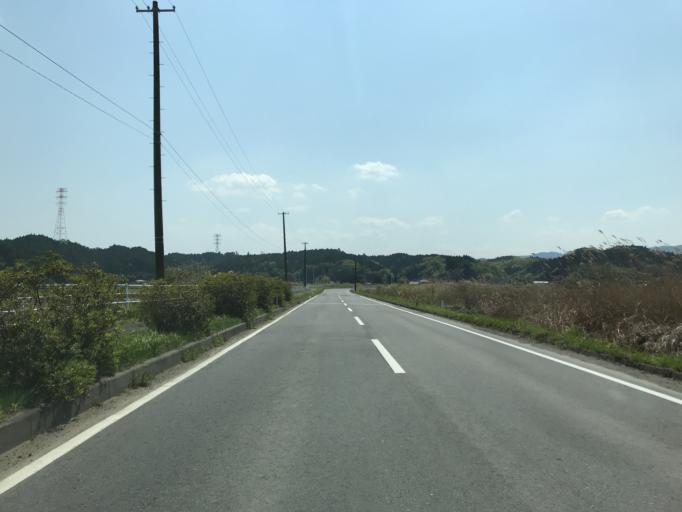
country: JP
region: Ibaraki
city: Kitaibaraki
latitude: 36.9235
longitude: 140.7509
